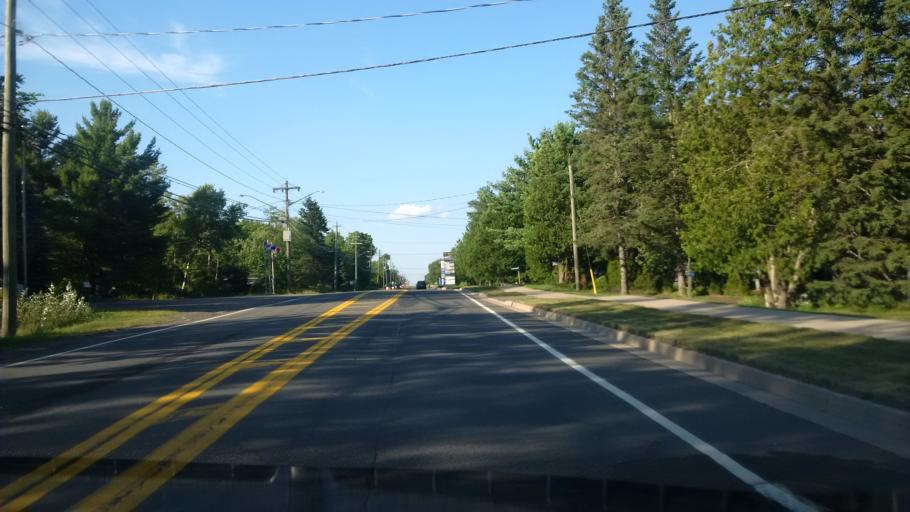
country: CA
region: New Brunswick
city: Fredericton
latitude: 45.8867
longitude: -66.6876
